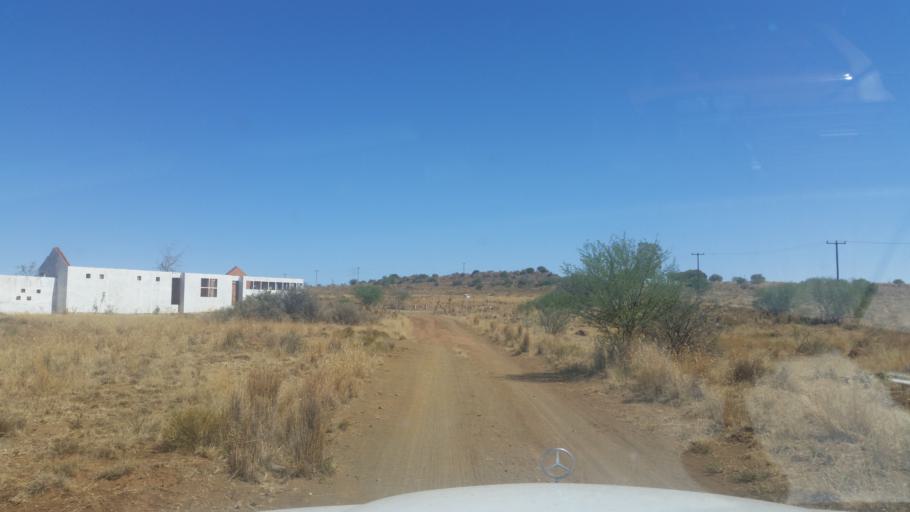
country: ZA
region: Eastern Cape
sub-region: Joe Gqabi District Municipality
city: Burgersdorp
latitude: -30.6943
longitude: 25.7792
